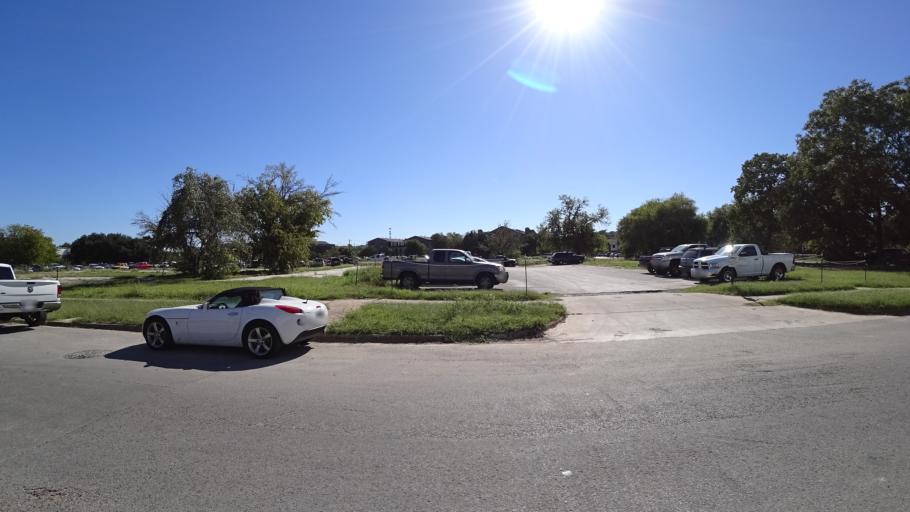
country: US
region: Texas
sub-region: Travis County
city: Austin
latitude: 30.2406
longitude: -97.7233
